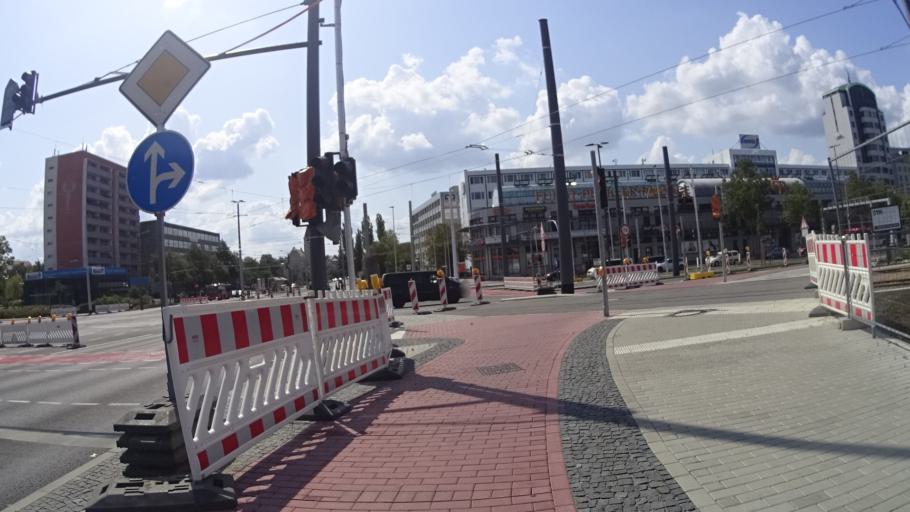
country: DE
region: Brandenburg
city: Cottbus
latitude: 51.7497
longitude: 14.3283
